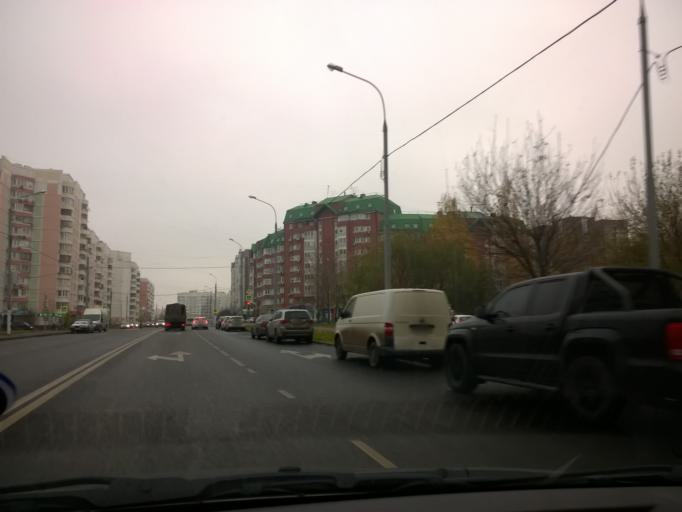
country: RU
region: Moskovskaya
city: Kommunarka
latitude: 55.5336
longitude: 37.5155
